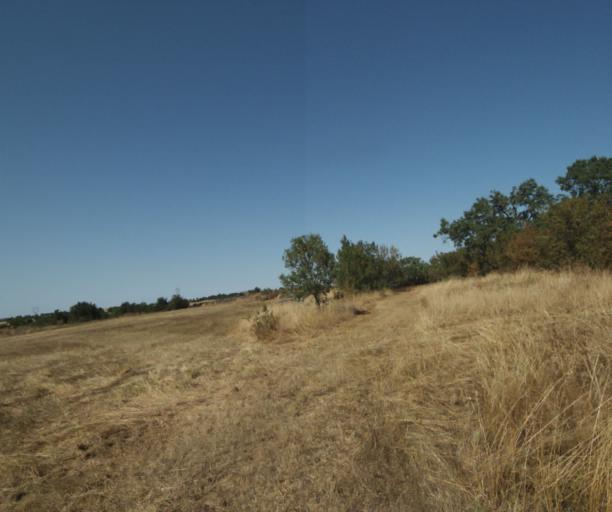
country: FR
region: Midi-Pyrenees
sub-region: Departement de la Haute-Garonne
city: Saint-Felix-Lauragais
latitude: 43.4423
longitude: 1.8282
